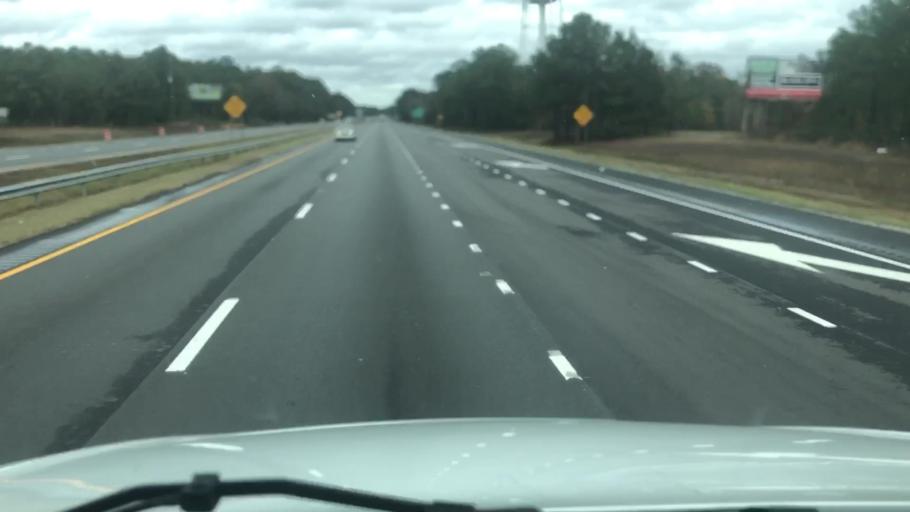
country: US
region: North Carolina
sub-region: Cumberland County
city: Eastover
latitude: 35.0972
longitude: -78.7762
